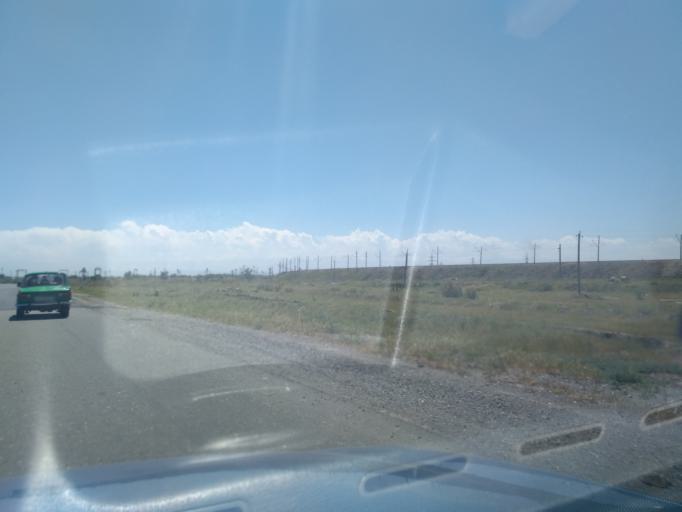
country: TJ
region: Viloyati Sughd
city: Zafarobod
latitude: 40.2152
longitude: 68.8566
